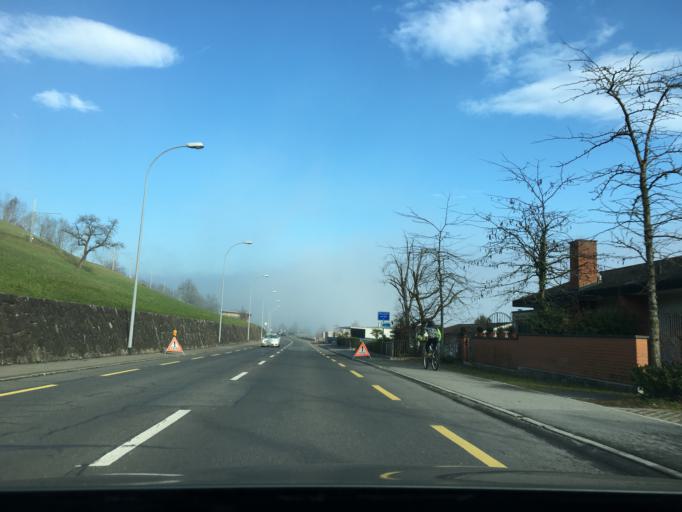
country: CH
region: Schwyz
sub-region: Bezirk Kuessnacht
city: Kussnacht
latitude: 47.0758
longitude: 8.4271
